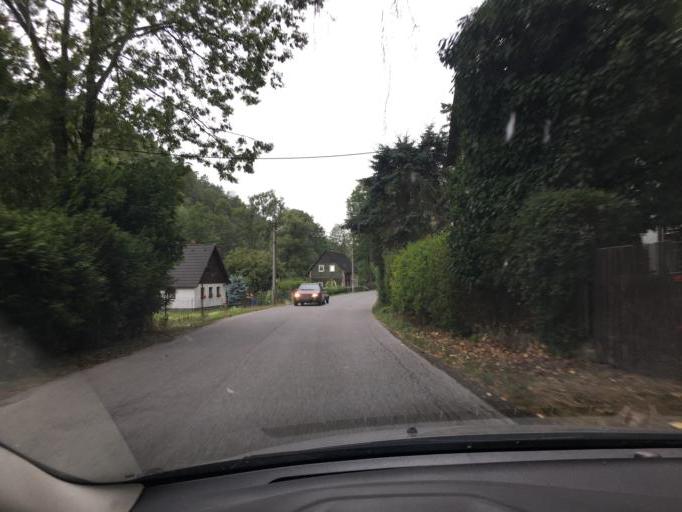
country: CZ
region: Ustecky
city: Ceska Kamenice
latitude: 50.8096
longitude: 14.3591
